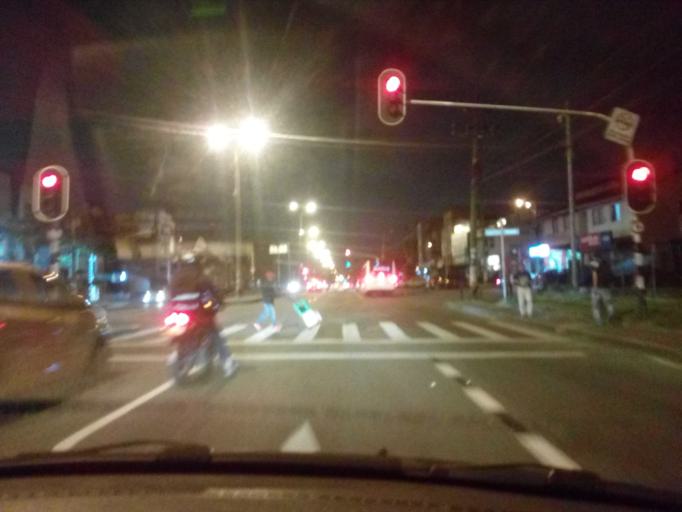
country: CO
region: Antioquia
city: Itagui
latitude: 6.1979
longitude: -75.5898
